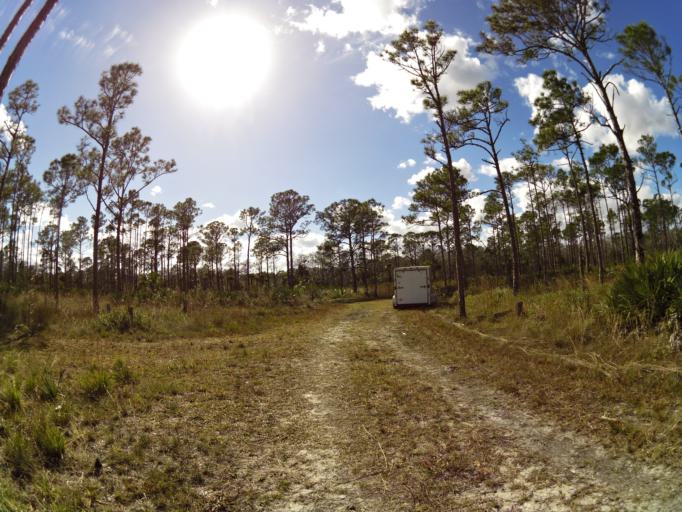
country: US
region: Florida
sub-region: Martin County
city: Hobe Sound
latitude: 27.0160
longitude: -80.1584
